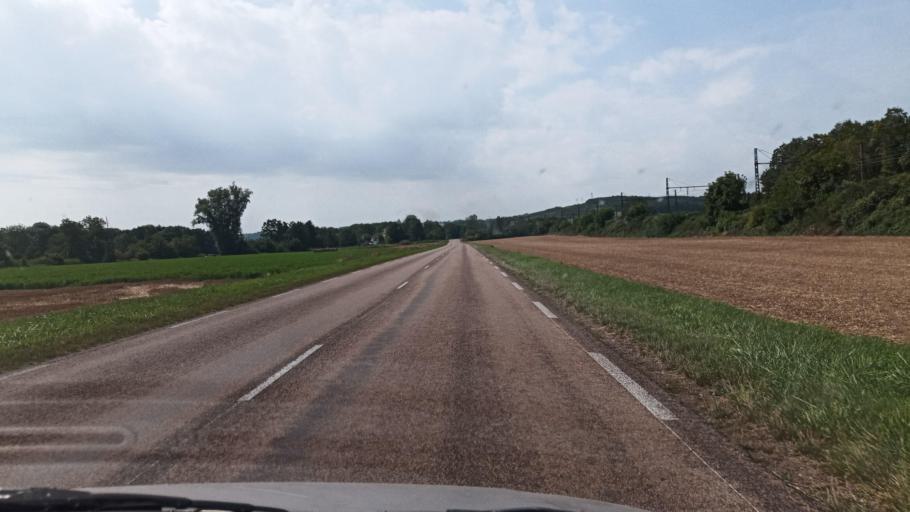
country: FR
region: Bourgogne
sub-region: Departement de l'Yonne
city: Veron
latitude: 48.1185
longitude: 3.2732
